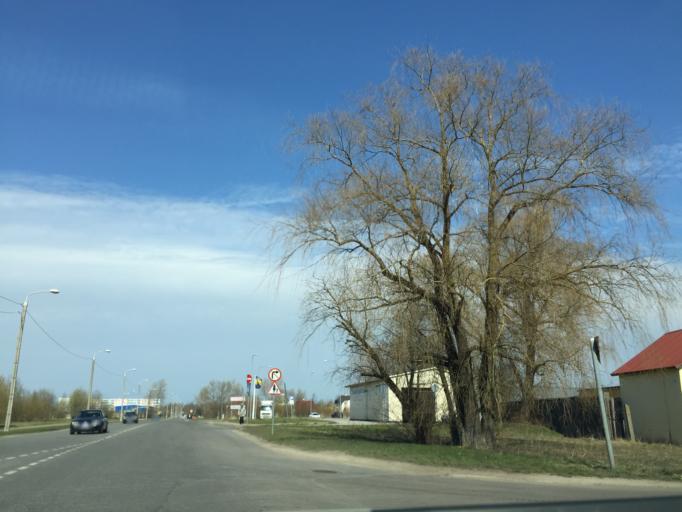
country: EE
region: Ida-Virumaa
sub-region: Narva linn
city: Narva
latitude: 59.3878
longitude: 28.1881
